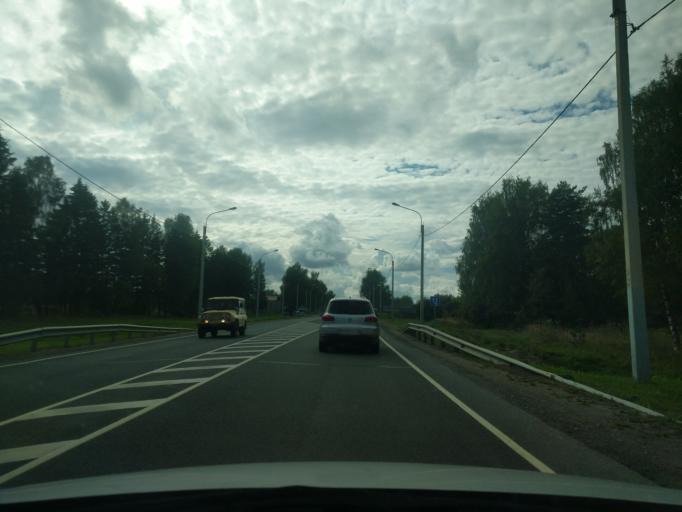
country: RU
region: Jaroslavl
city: Levashevo
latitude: 57.6462
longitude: 40.5419
